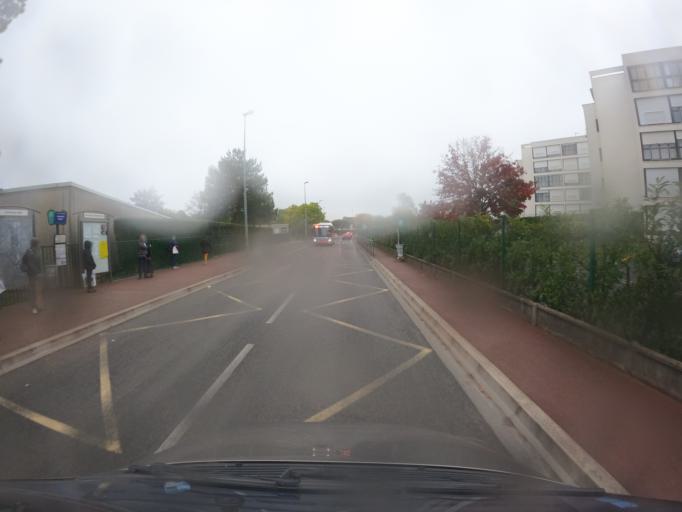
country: FR
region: Ile-de-France
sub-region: Departement du Val-de-Marne
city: Chennevieres-sur-Marne
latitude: 48.7993
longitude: 2.5535
